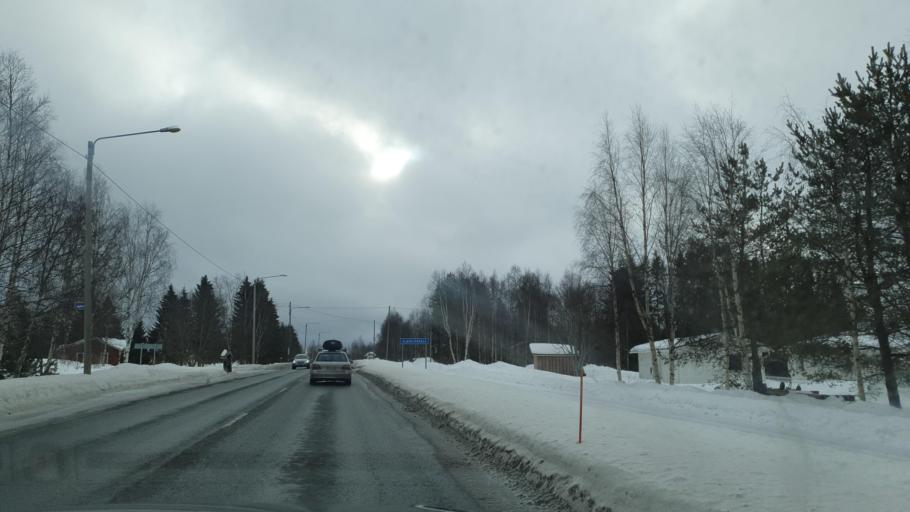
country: FI
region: Lapland
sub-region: Kemi-Tornio
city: Tornio
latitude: 65.9282
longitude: 24.1268
